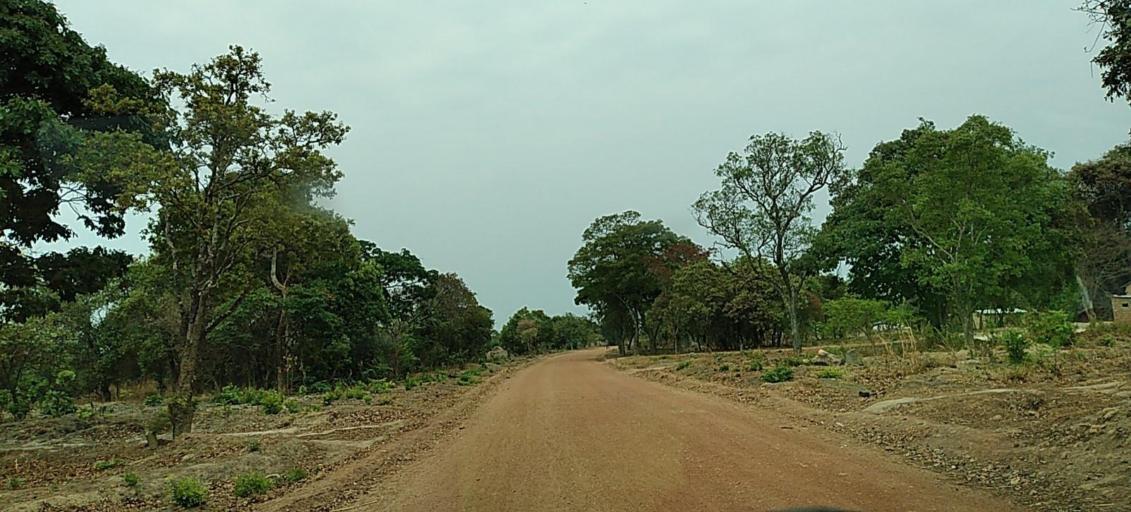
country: ZM
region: North-Western
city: Solwezi
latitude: -12.4749
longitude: 26.5306
